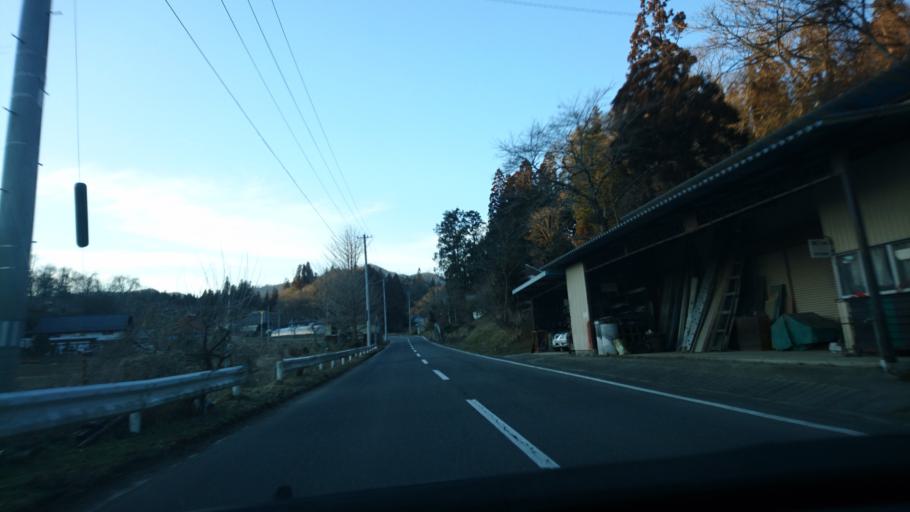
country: JP
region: Iwate
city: Mizusawa
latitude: 39.0426
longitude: 141.3404
